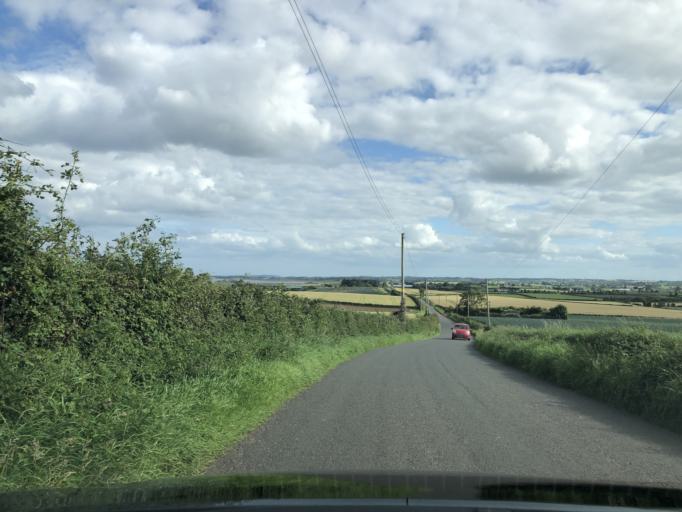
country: GB
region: Northern Ireland
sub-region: Ards District
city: Newtownards
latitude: 54.5688
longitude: -5.7129
